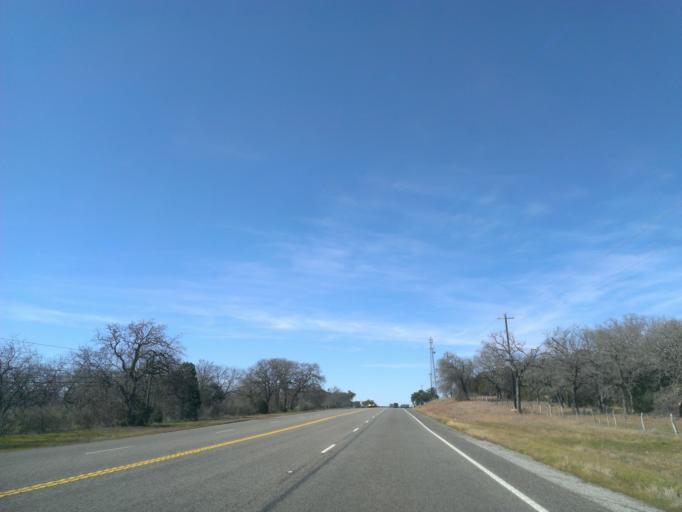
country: US
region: Texas
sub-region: Burnet County
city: Marble Falls
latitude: 30.4780
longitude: -98.1911
